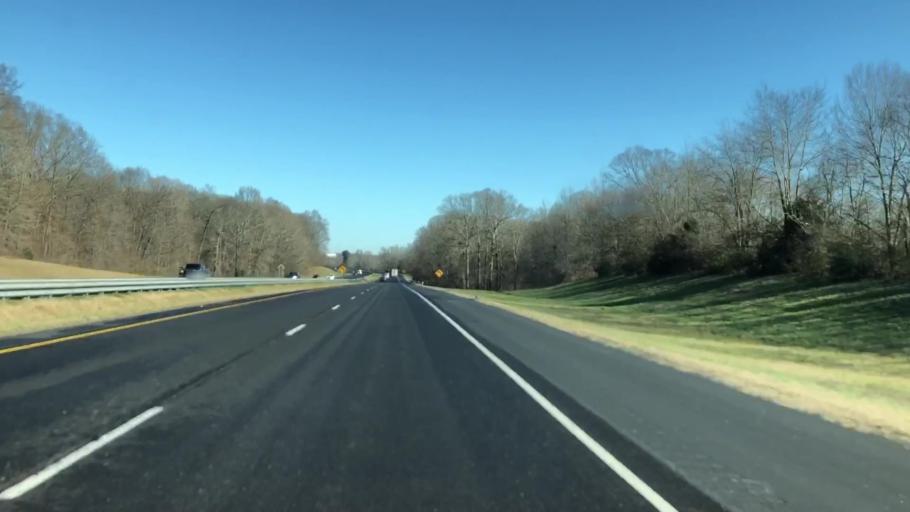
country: US
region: Alabama
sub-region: Limestone County
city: Athens
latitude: 34.8954
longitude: -86.9108
